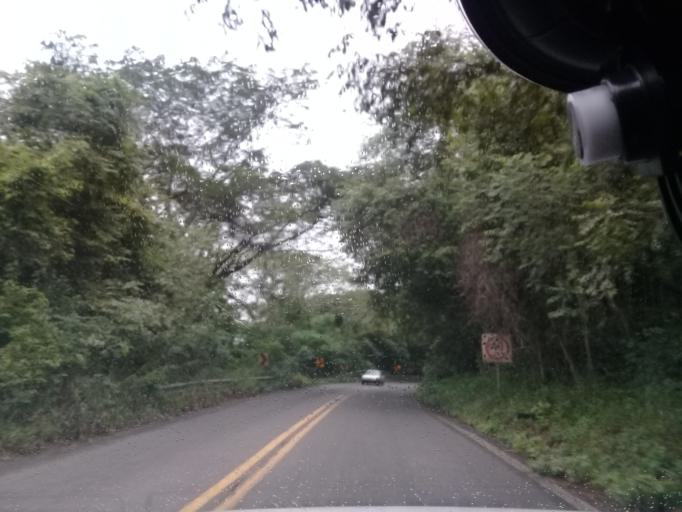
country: MX
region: Veracruz
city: Platon Sanchez
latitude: 21.2404
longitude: -98.3673
